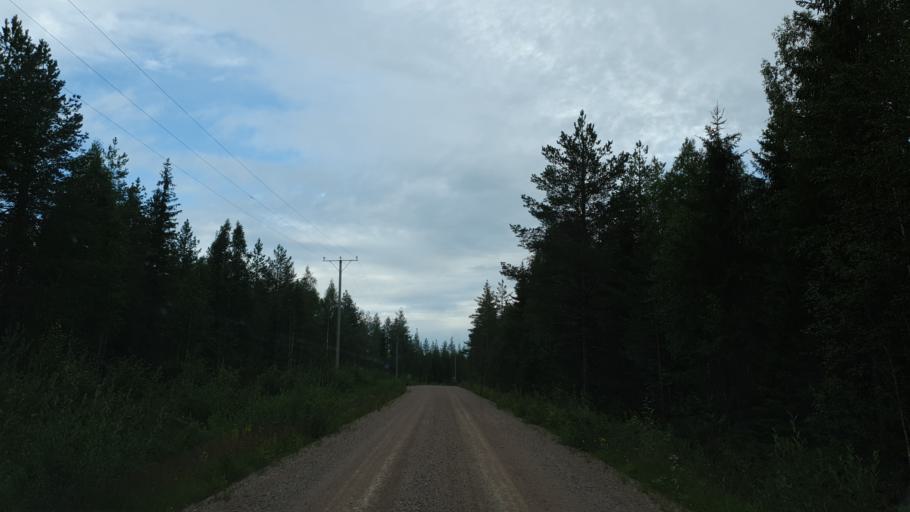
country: FI
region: Kainuu
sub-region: Kehys-Kainuu
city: Suomussalmi
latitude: 64.4487
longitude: 28.9690
